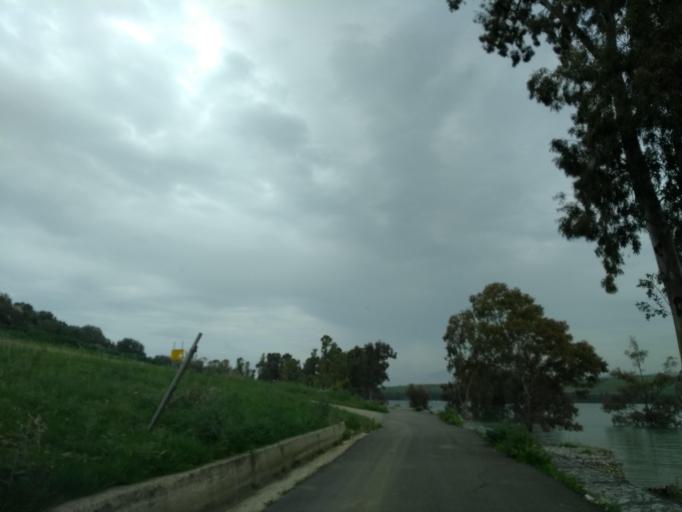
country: IT
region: Sicily
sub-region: Palermo
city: Partinico
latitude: 37.9945
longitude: 13.0823
